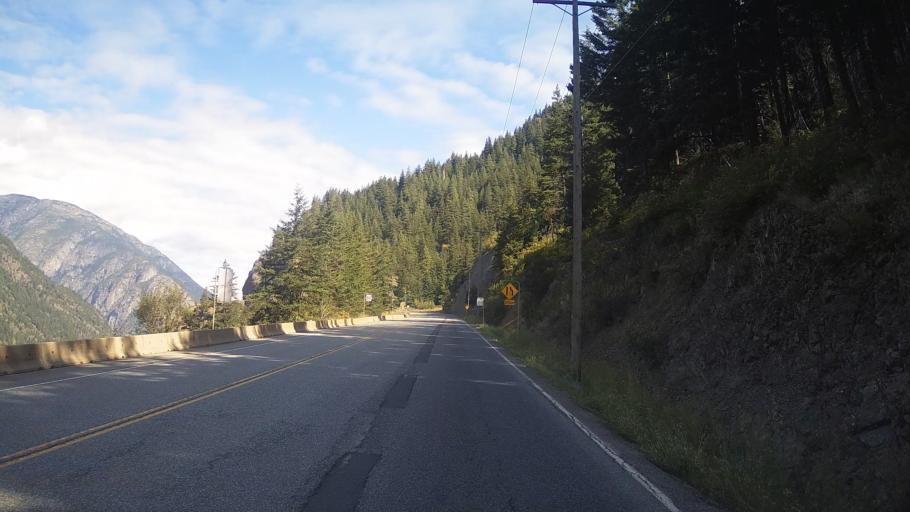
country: CA
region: British Columbia
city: Hope
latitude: 50.0720
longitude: -121.5465
